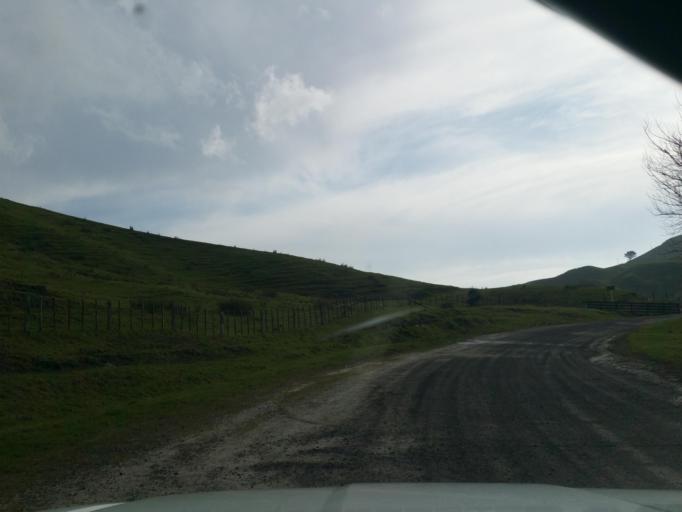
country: NZ
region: Northland
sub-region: Kaipara District
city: Dargaville
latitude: -35.8634
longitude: 173.7204
